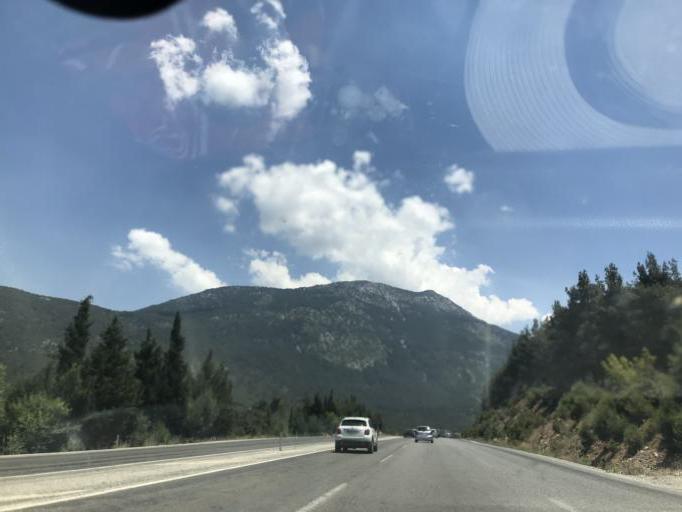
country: TR
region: Denizli
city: Honaz
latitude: 37.7261
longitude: 29.2029
